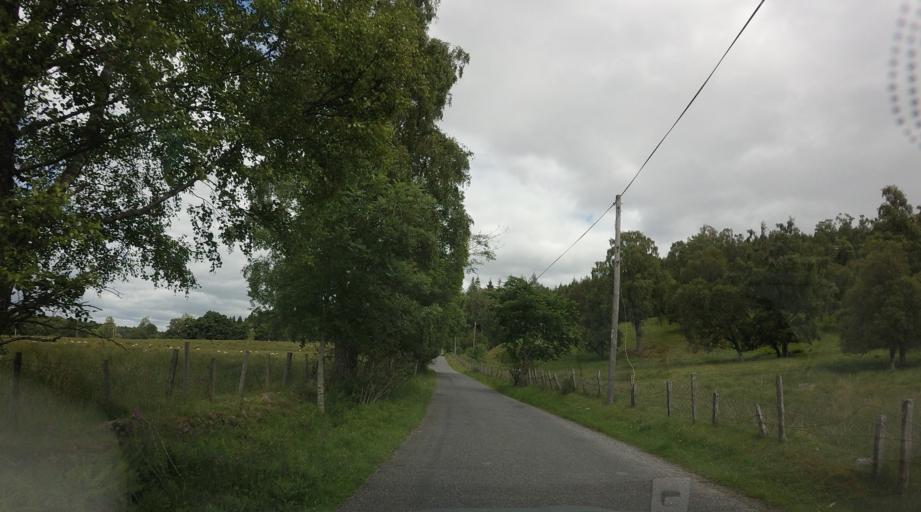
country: GB
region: Scotland
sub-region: Perth and Kinross
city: Aberfeldy
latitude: 56.6930
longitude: -4.1279
